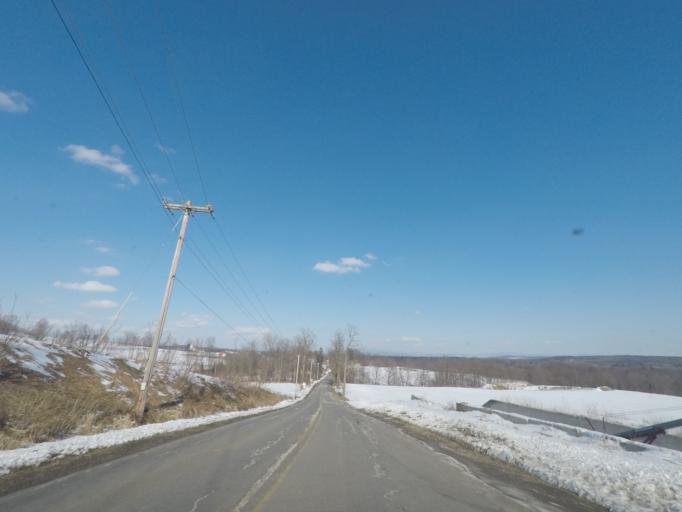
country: US
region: New York
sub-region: Saratoga County
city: Stillwater
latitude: 42.9184
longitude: -73.5393
